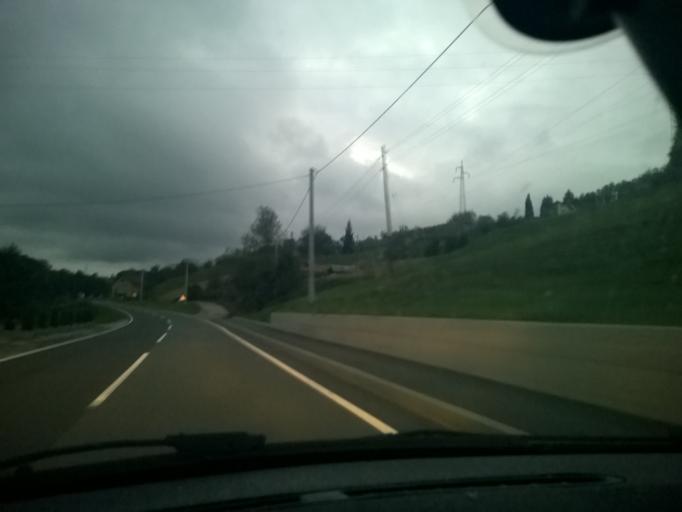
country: HR
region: Krapinsko-Zagorska
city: Pregrada
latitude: 46.2088
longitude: 15.7863
